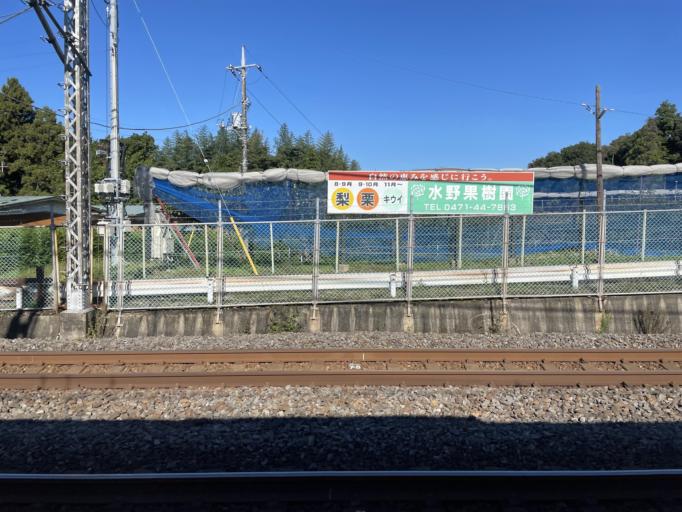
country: JP
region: Chiba
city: Kashiwa
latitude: 35.8371
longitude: 139.9383
